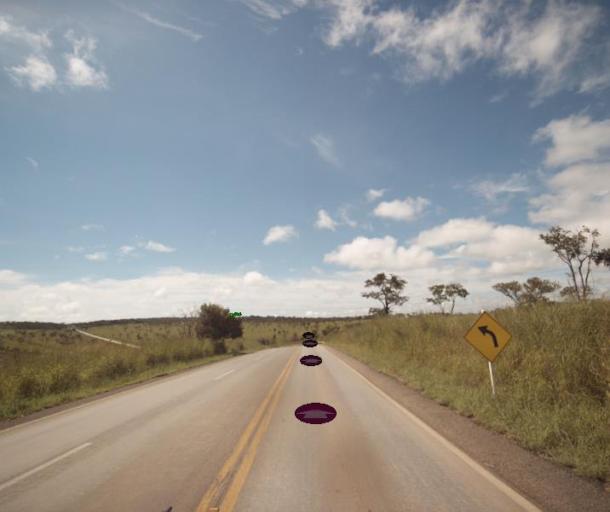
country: BR
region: Goias
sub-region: Padre Bernardo
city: Padre Bernardo
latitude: -15.2110
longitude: -48.4774
